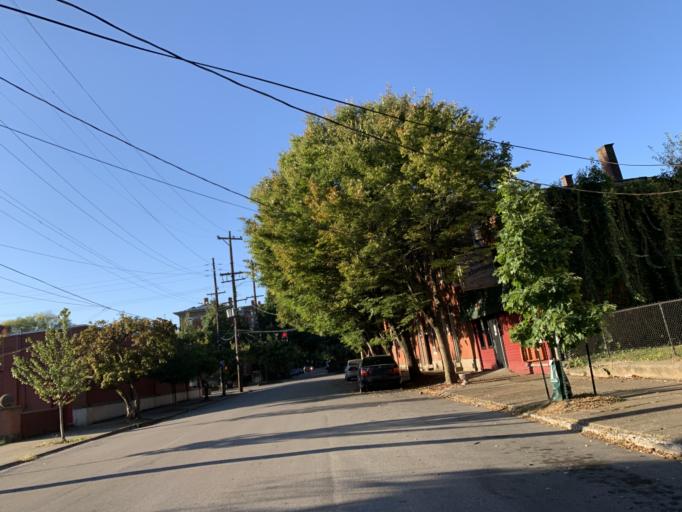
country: US
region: Kentucky
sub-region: Jefferson County
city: Louisville
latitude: 38.2358
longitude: -85.7619
